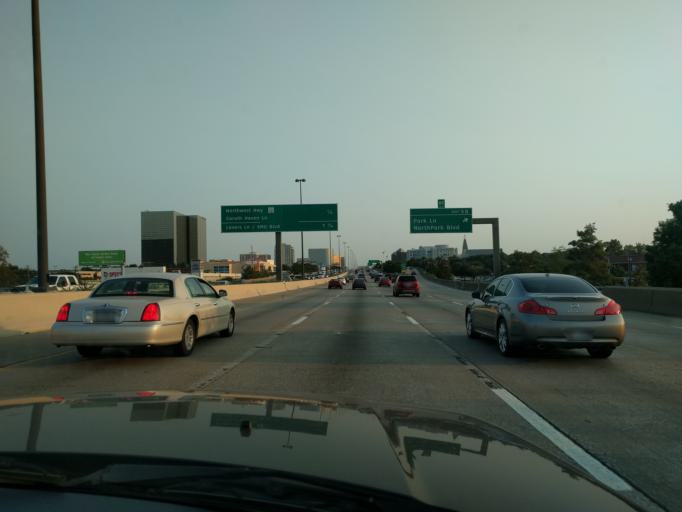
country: US
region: Texas
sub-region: Dallas County
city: University Park
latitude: 32.8811
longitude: -96.7703
